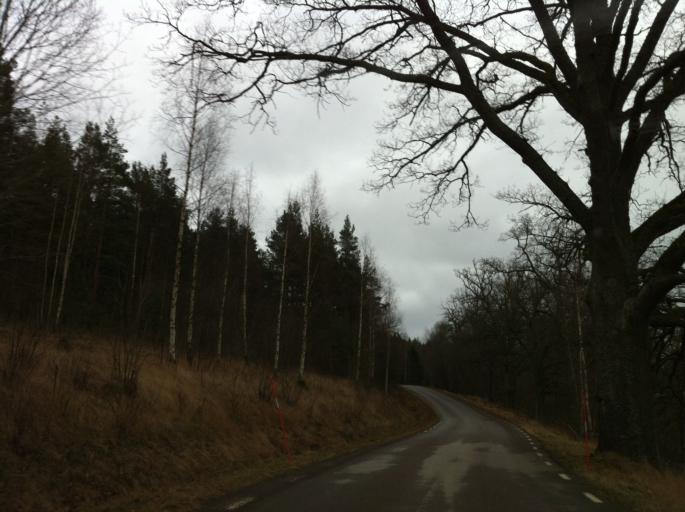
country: SE
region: Kalmar
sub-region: Vasterviks Kommun
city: Vaestervik
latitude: 57.9083
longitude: 16.6601
